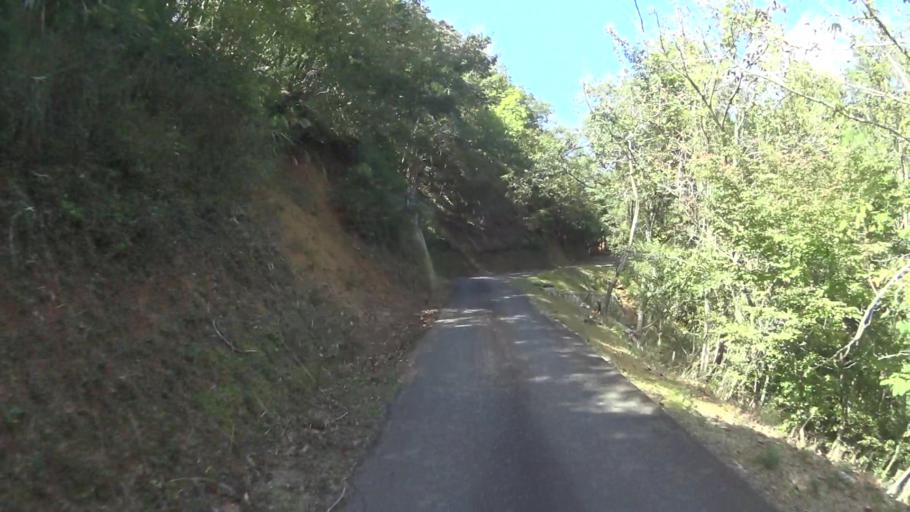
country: JP
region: Hyogo
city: Toyooka
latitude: 35.6063
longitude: 134.9964
